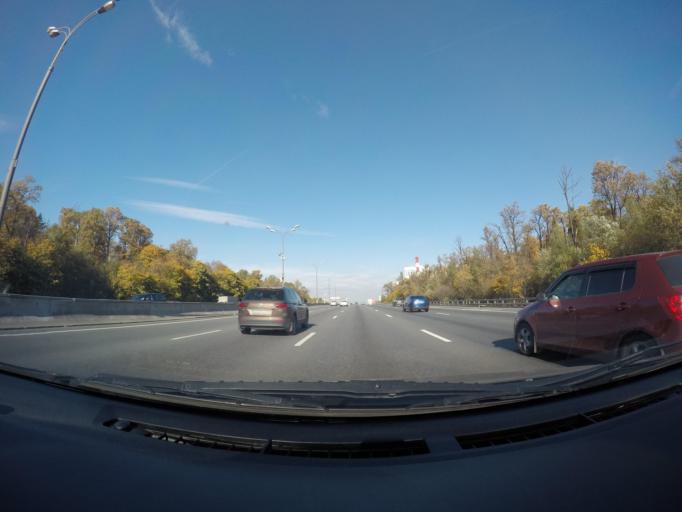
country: RU
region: Moscow
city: Vostochnyy
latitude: 55.7995
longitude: 37.8404
